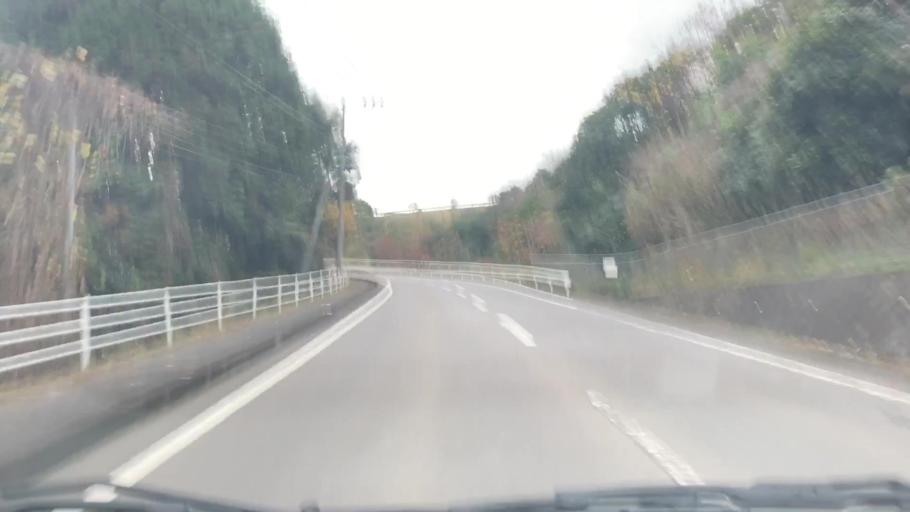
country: JP
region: Saga Prefecture
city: Ureshinomachi-shimojuku
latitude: 33.1138
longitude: 129.9760
